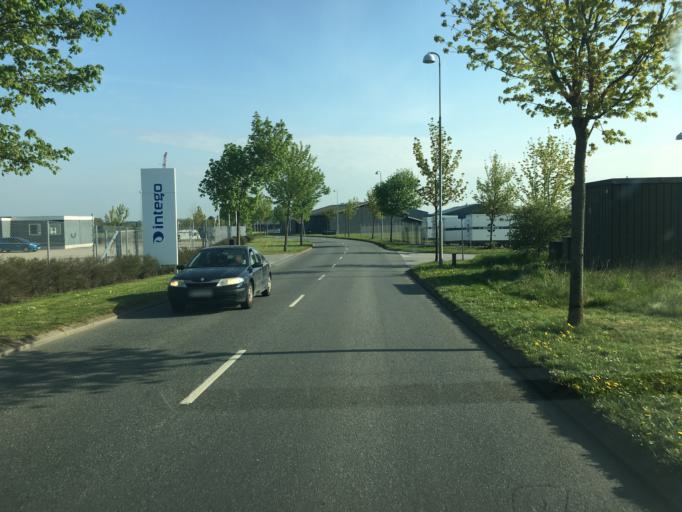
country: DK
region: South Denmark
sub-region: Aabenraa Kommune
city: Rodekro
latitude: 55.0709
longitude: 9.3628
